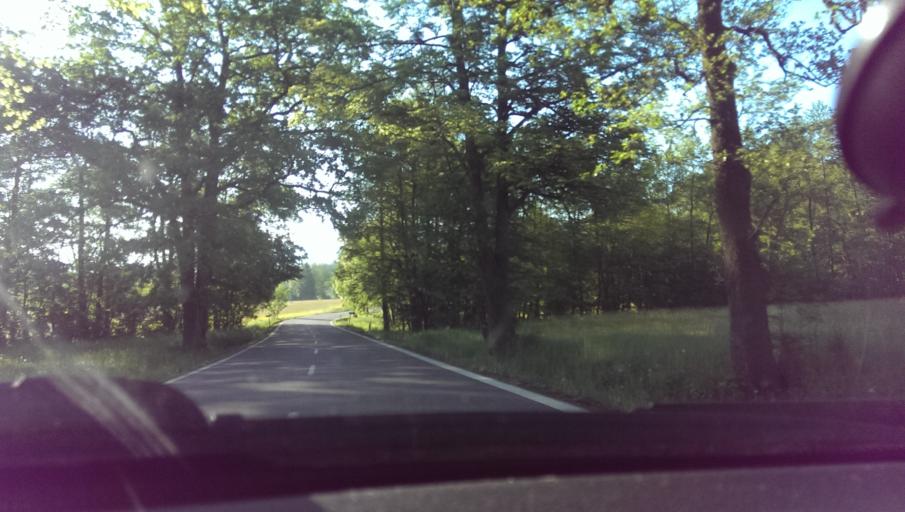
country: CZ
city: Kuncice pod Ondrejnikem
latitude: 49.5463
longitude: 18.2589
